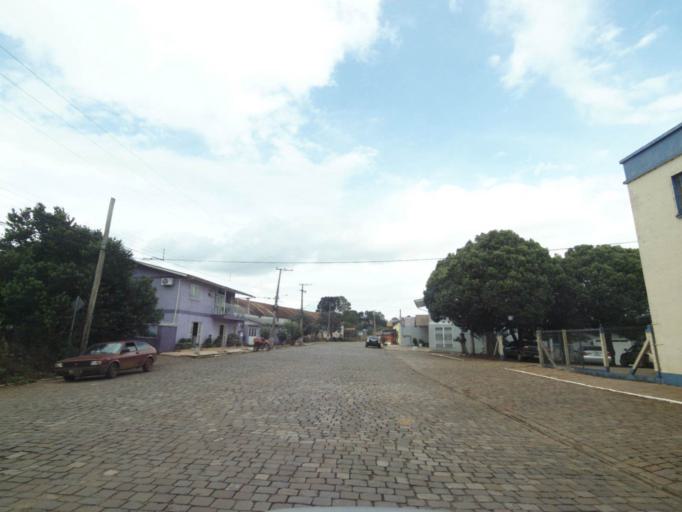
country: BR
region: Rio Grande do Sul
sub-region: Lagoa Vermelha
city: Lagoa Vermelha
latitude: -28.2084
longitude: -51.5405
